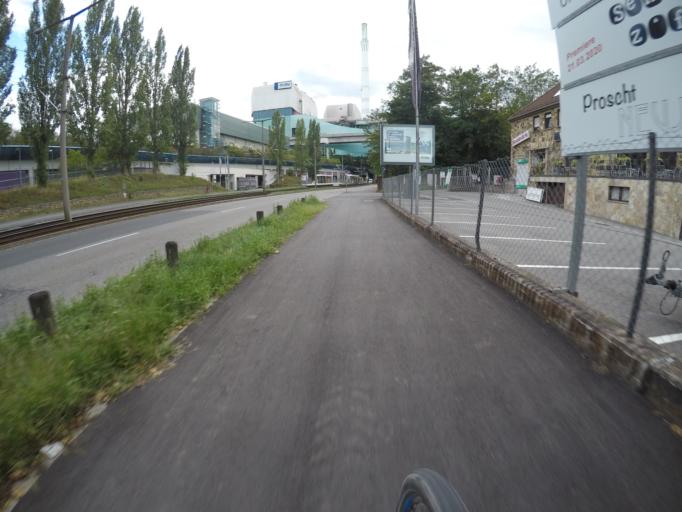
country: DE
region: Baden-Wuerttemberg
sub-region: Regierungsbezirk Stuttgart
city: Stuttgart Muehlhausen
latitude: 48.8172
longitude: 9.2232
